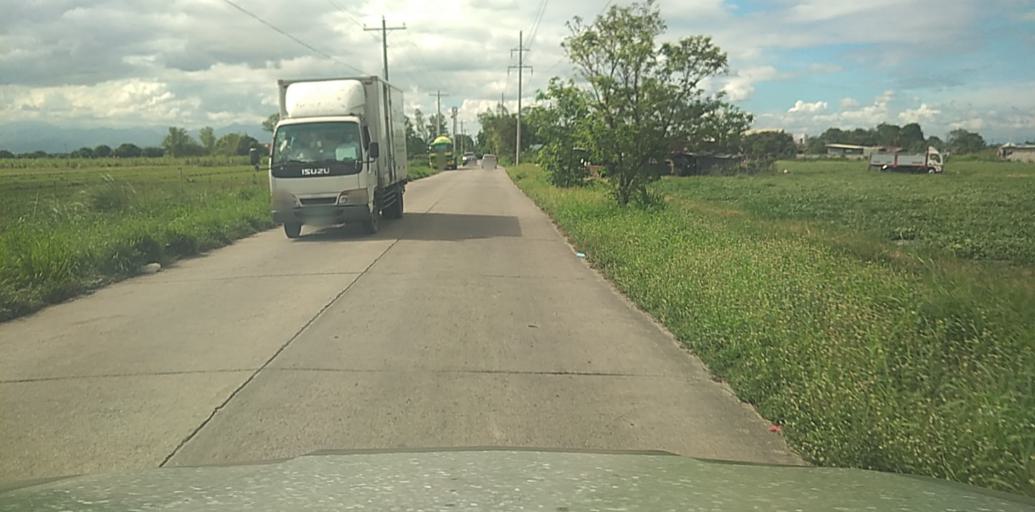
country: PH
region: Central Luzon
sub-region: Province of Pampanga
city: Arenas
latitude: 15.1750
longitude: 120.6705
